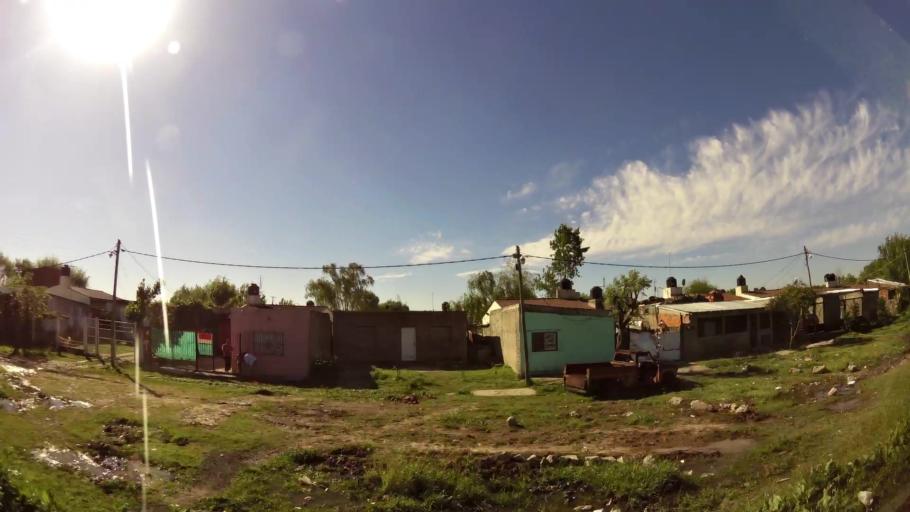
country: AR
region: Buenos Aires
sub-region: Partido de Quilmes
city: Quilmes
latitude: -34.7593
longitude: -58.3114
